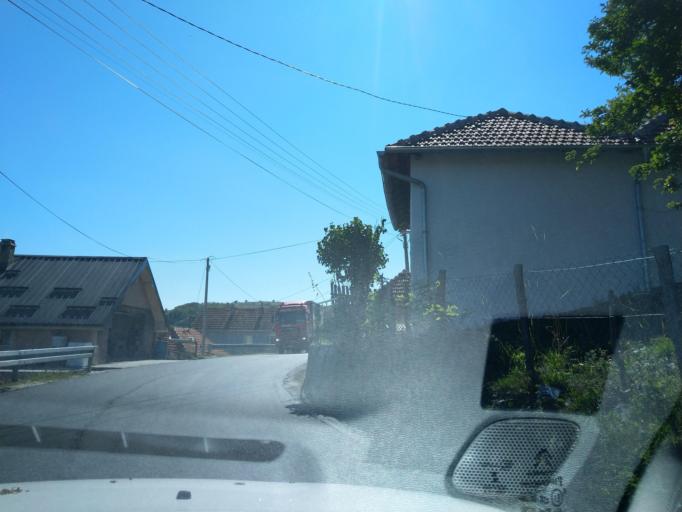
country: RS
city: Sokolovica
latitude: 43.2548
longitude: 20.2295
